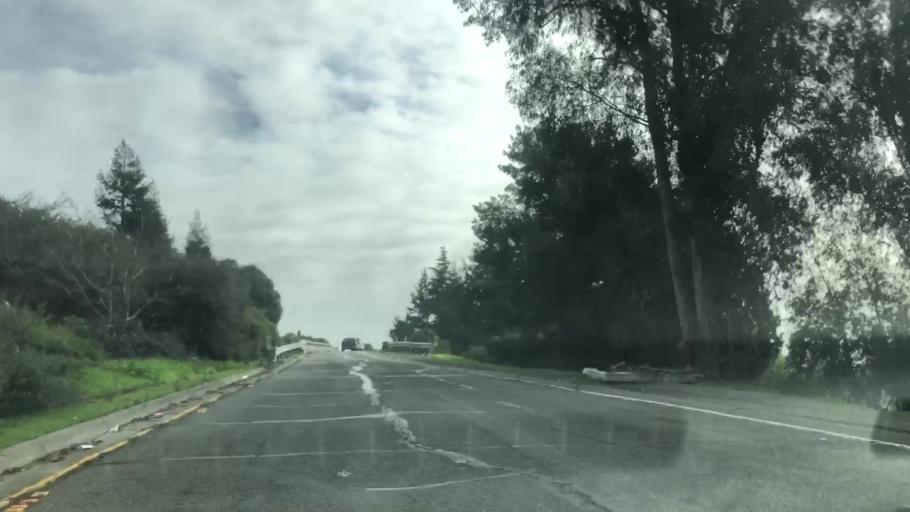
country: US
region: California
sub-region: Alameda County
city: Ashland
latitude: 37.7000
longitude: -122.1093
